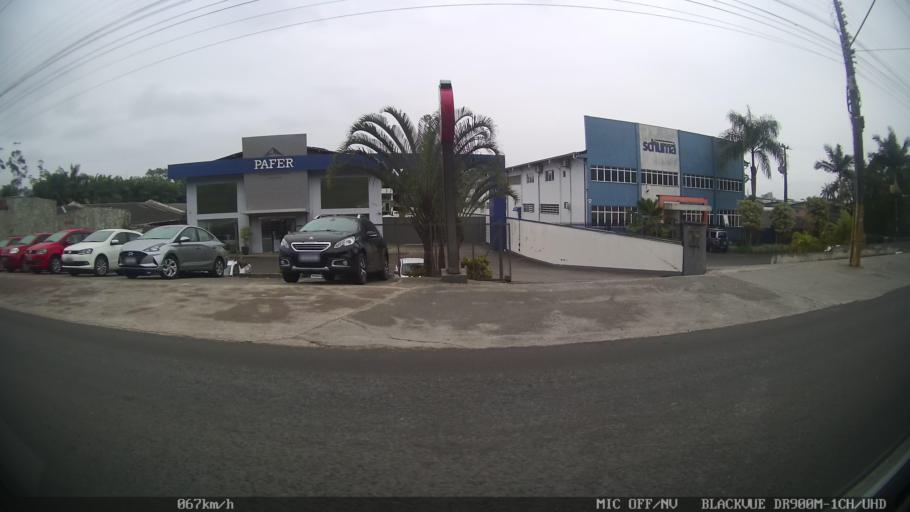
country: BR
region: Santa Catarina
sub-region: Joinville
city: Joinville
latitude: -26.2459
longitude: -48.8398
